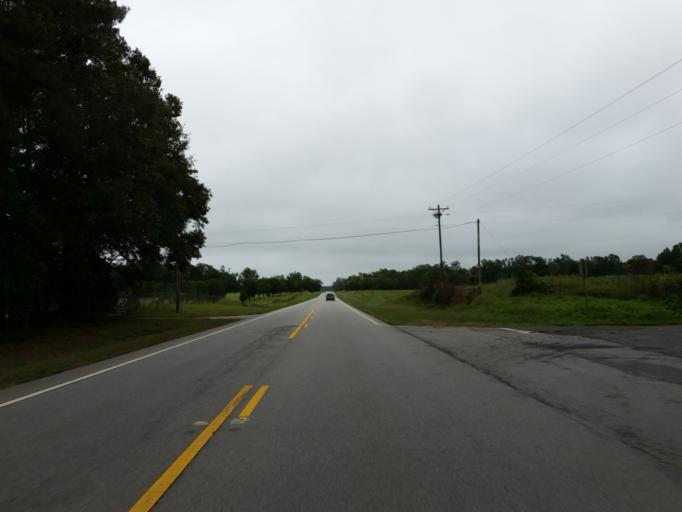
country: US
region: Georgia
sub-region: Lamar County
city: Barnesville
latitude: 32.9900
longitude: -84.1215
